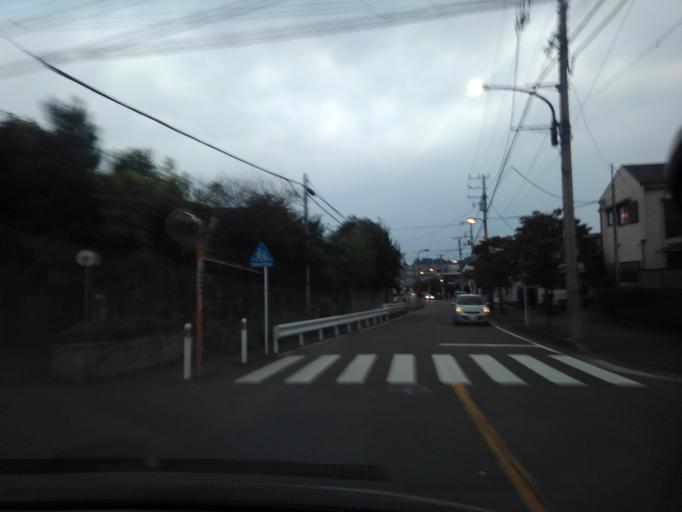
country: JP
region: Tokyo
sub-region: Machida-shi
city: Machida
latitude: 35.5812
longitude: 139.3919
